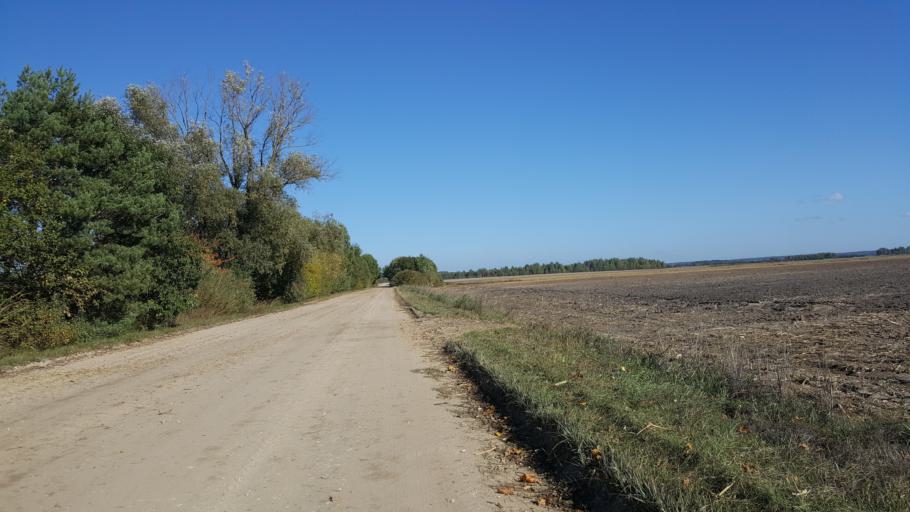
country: BY
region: Brest
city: Kamyanyets
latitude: 52.4258
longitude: 23.8801
